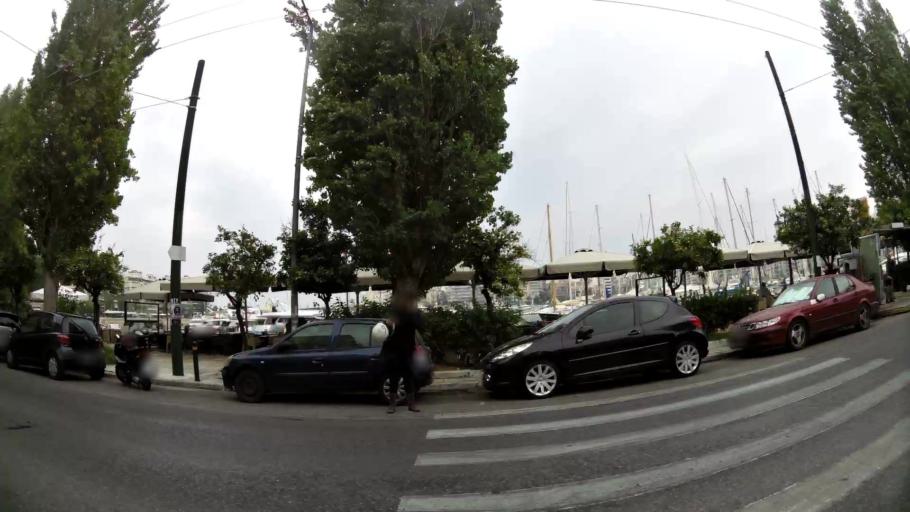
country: GR
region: Attica
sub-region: Nomos Attikis
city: Piraeus
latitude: 37.9386
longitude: 23.6501
